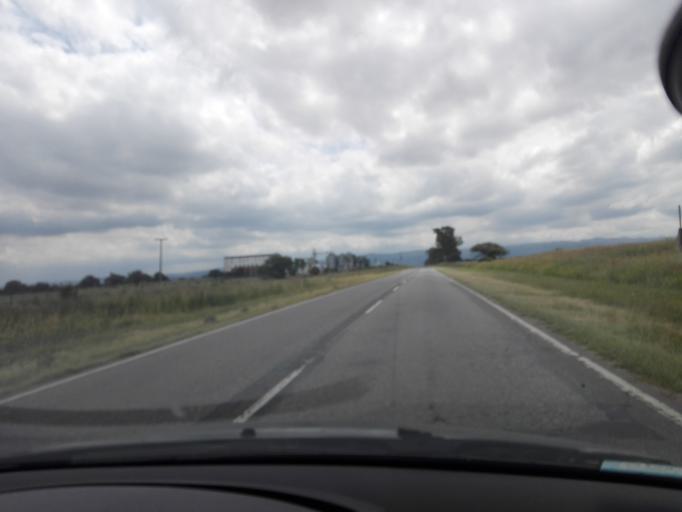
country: AR
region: Cordoba
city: Alta Gracia
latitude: -31.6581
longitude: -64.3719
